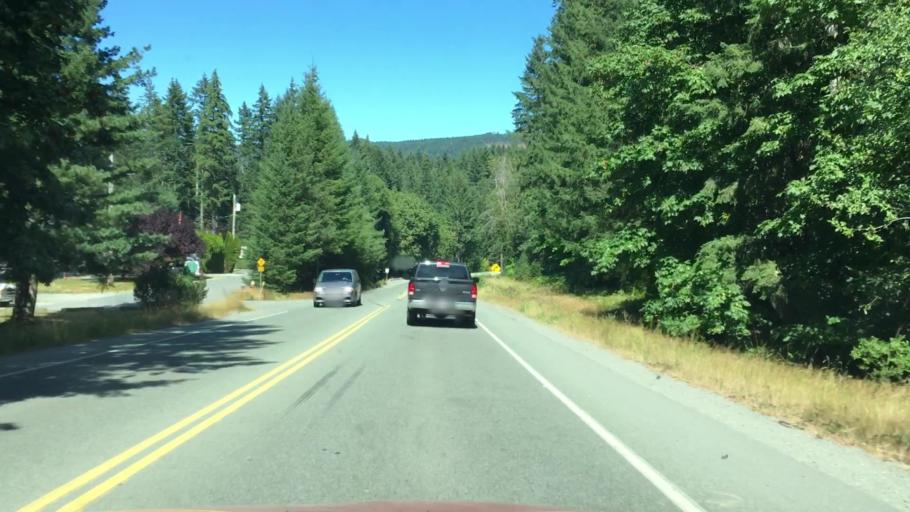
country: CA
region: British Columbia
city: Port Alberni
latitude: 49.2579
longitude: -124.7754
